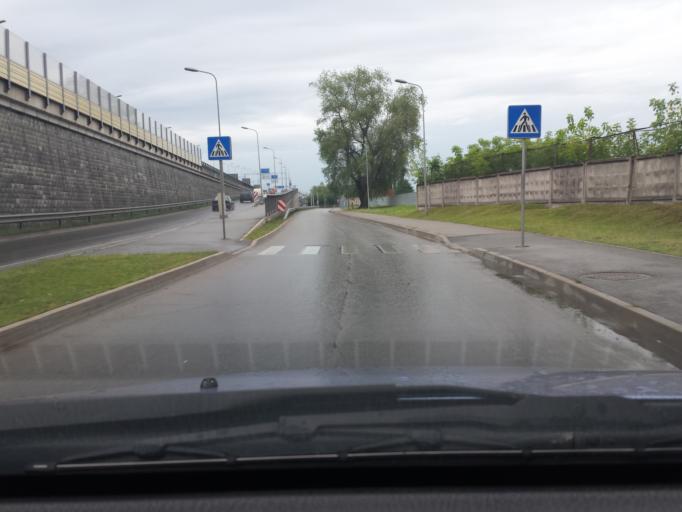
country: LV
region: Riga
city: Riga
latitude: 56.9245
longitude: 24.1717
